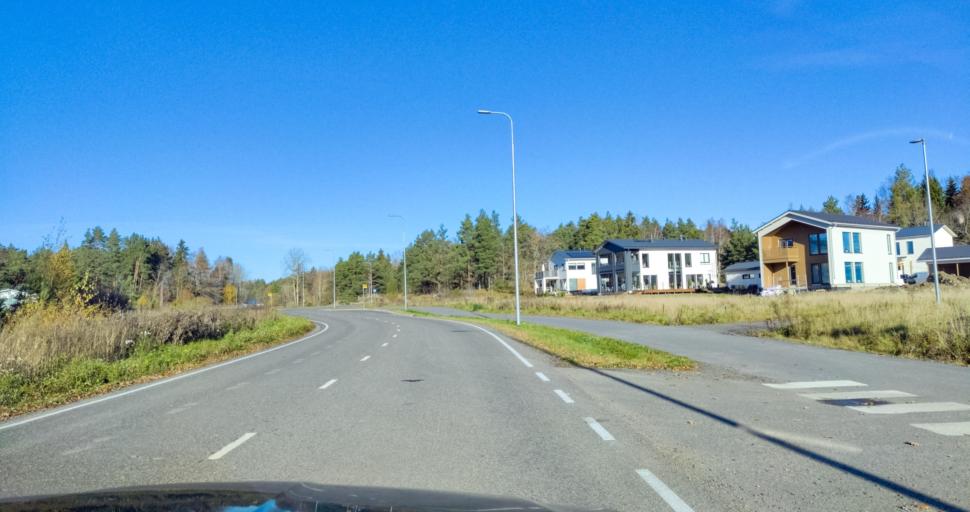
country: FI
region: Varsinais-Suomi
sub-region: Turku
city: Turku
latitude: 60.4062
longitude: 22.2084
